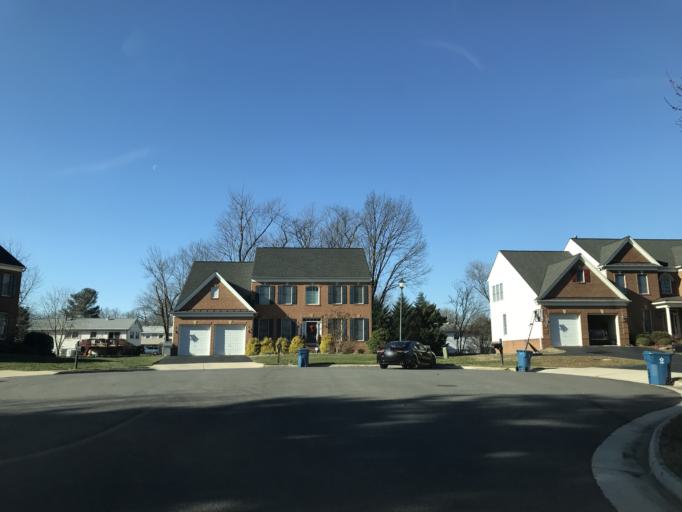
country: US
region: Virginia
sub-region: Fairfax County
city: Franconia
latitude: 38.7832
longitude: -77.1600
